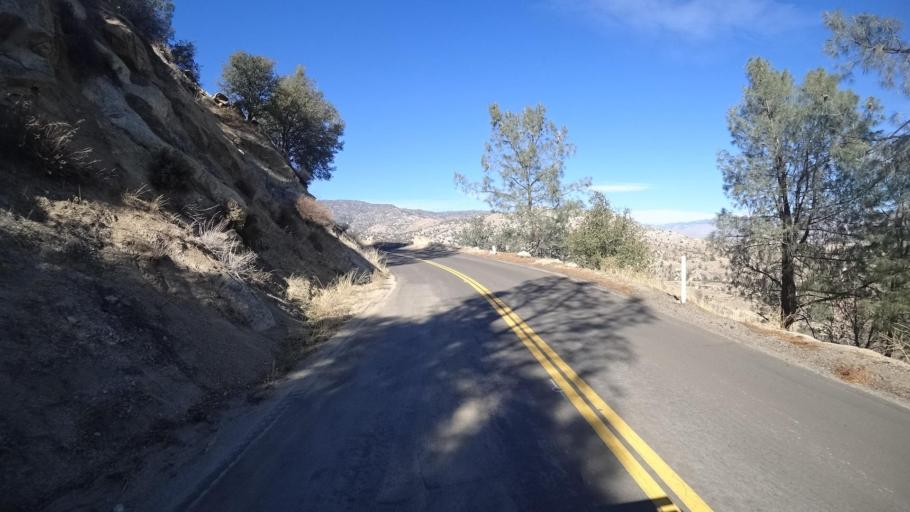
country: US
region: California
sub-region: Kern County
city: Bodfish
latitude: 35.5936
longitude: -118.5060
